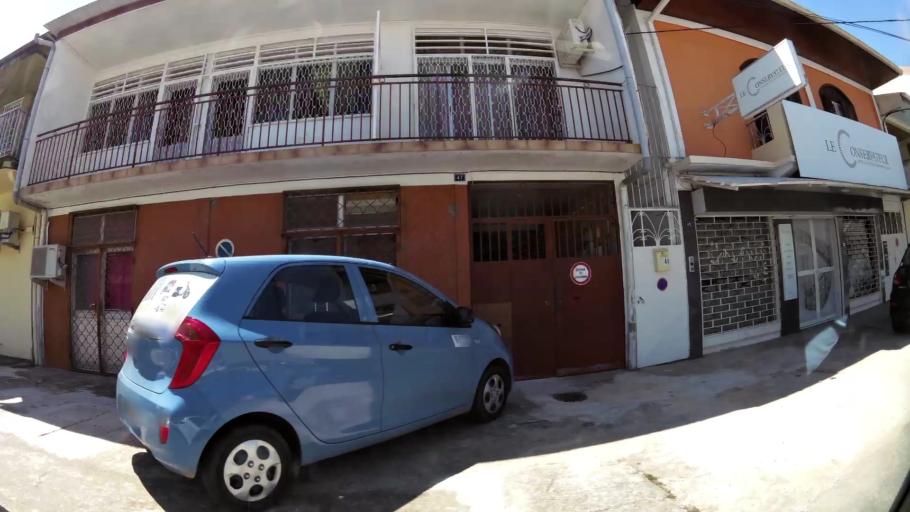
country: GF
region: Guyane
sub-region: Guyane
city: Cayenne
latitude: 4.9430
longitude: -52.3231
